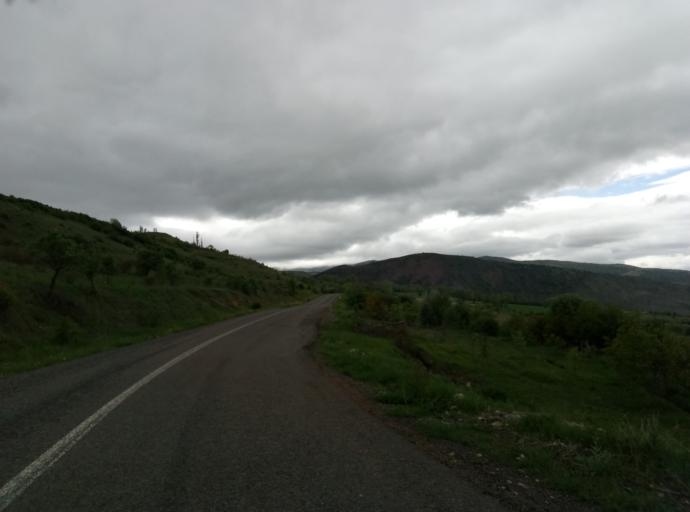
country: TR
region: Sivas
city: Aksu
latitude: 40.1880
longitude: 37.9481
